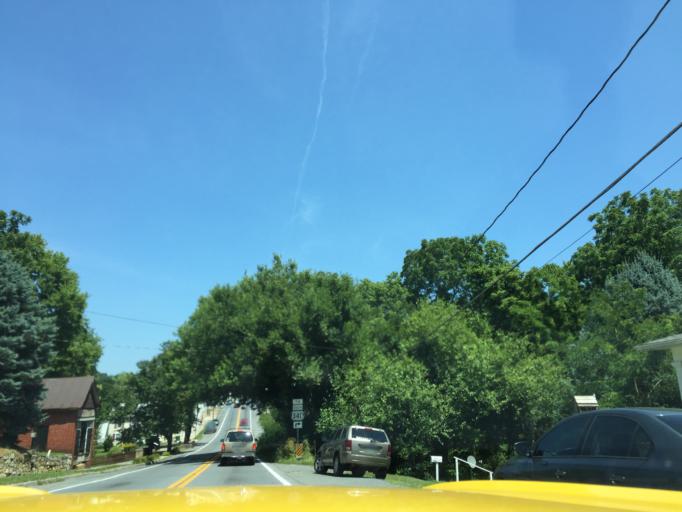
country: US
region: West Virginia
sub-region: Jefferson County
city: Charles Town
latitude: 39.2870
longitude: -77.8660
